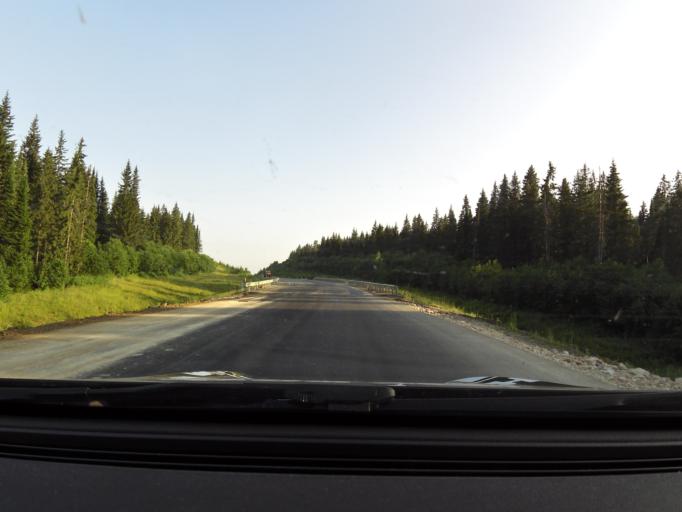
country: RU
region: Sverdlovsk
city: Nizhniye Sergi
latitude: 56.6672
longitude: 59.2686
